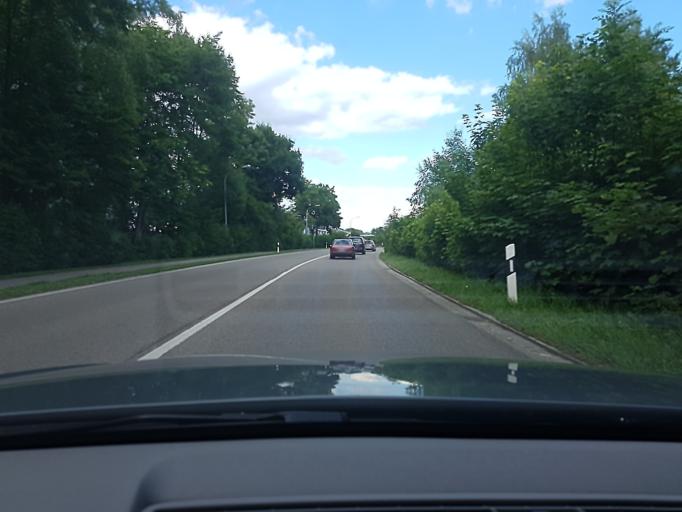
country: DE
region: Bavaria
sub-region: Swabia
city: Neu-Ulm
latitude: 48.4344
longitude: 10.0556
